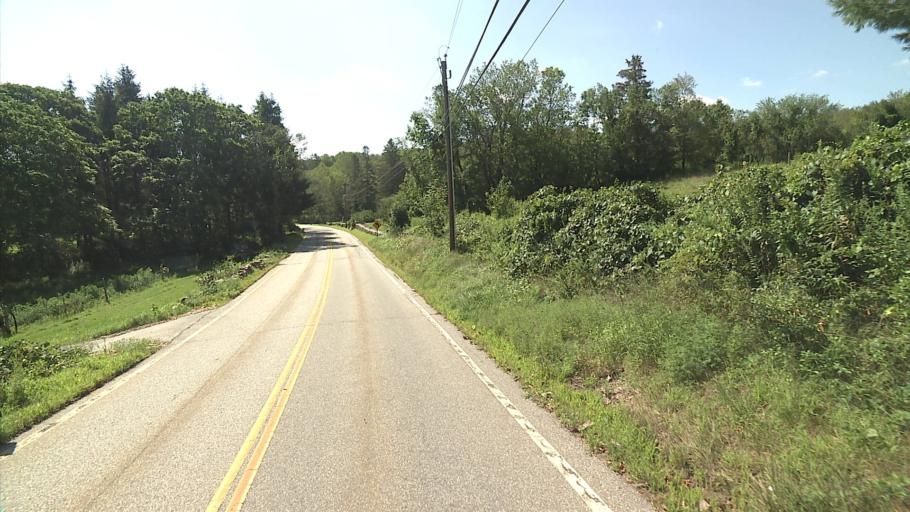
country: US
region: Connecticut
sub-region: Tolland County
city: Storrs
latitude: 41.8194
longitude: -72.1727
